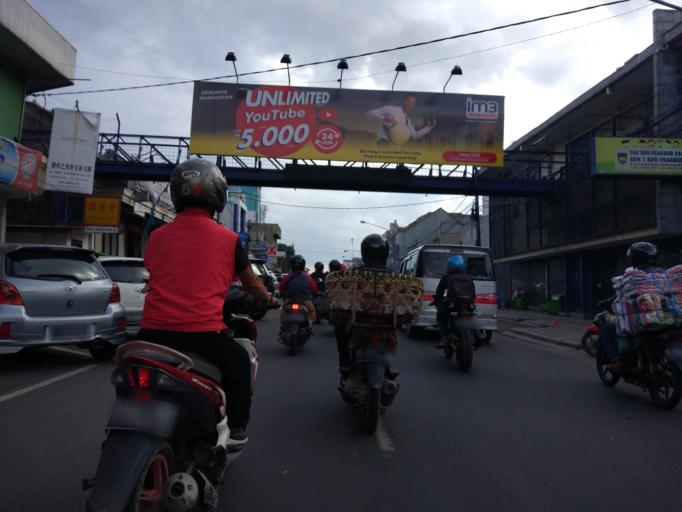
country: ID
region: West Java
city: Bandung
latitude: -6.9198
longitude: 107.5952
